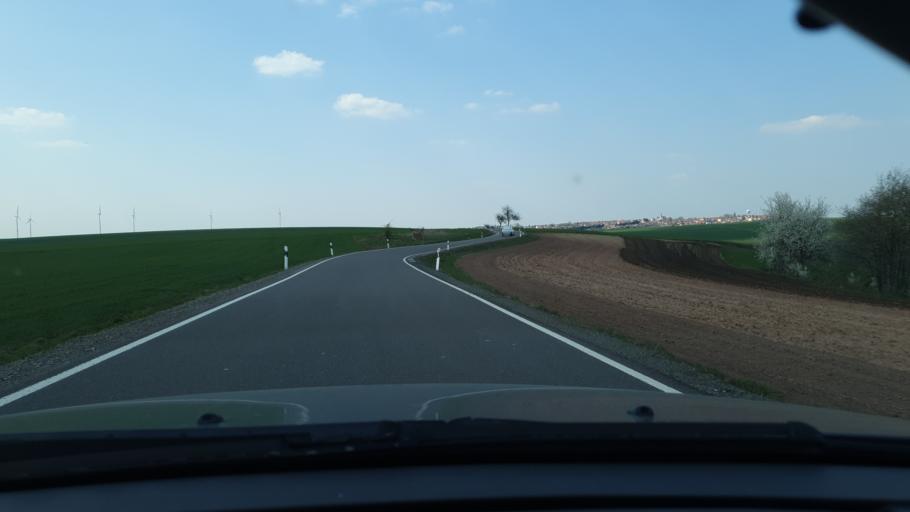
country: DE
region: Rheinland-Pfalz
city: Knopp-Labach
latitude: 49.3409
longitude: 7.4893
